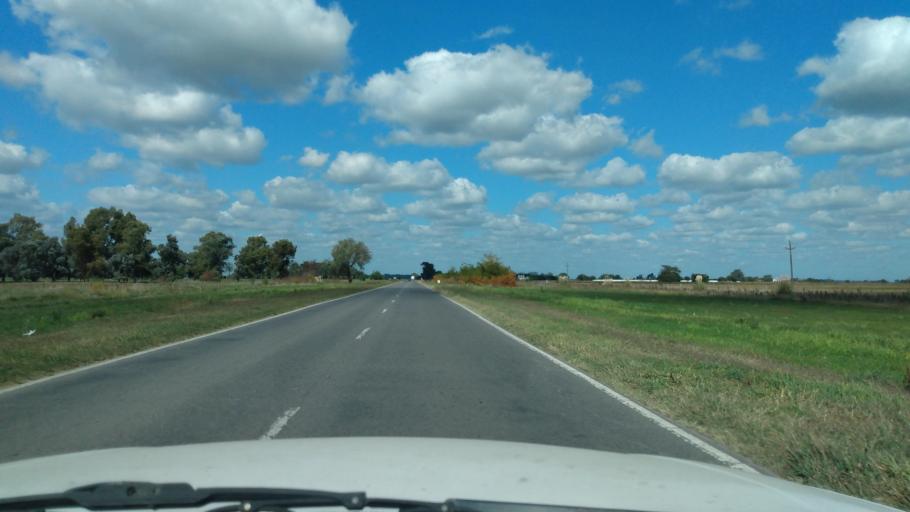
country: AR
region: Buenos Aires
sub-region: Partido de Navarro
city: Navarro
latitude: -34.9496
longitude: -59.3201
